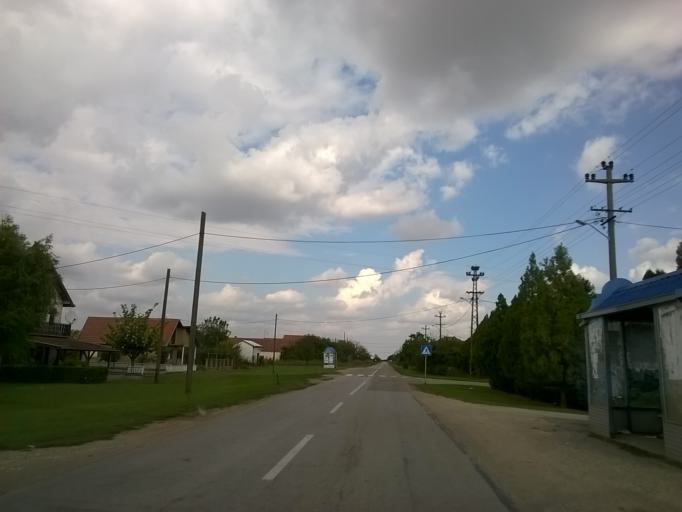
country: RS
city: Barice
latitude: 45.1828
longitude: 21.0783
